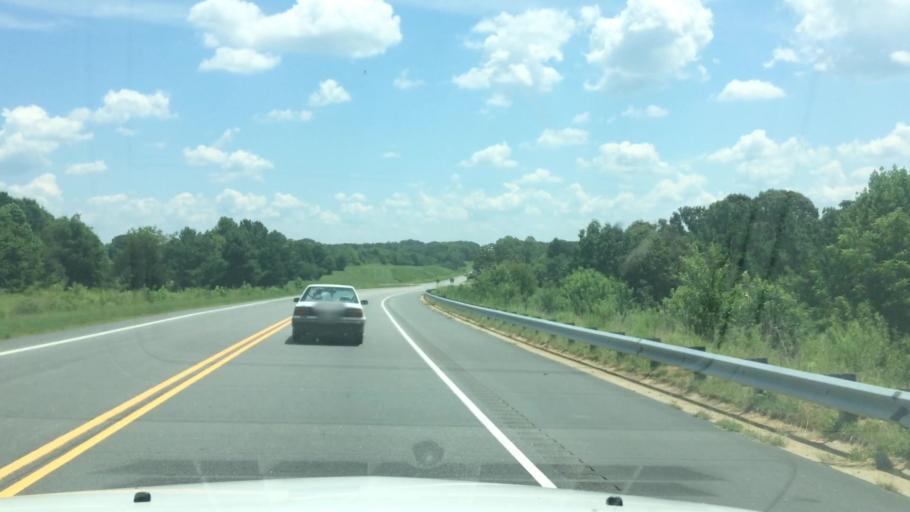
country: US
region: North Carolina
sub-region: Alexander County
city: Taylorsville
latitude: 35.9119
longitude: -81.1424
